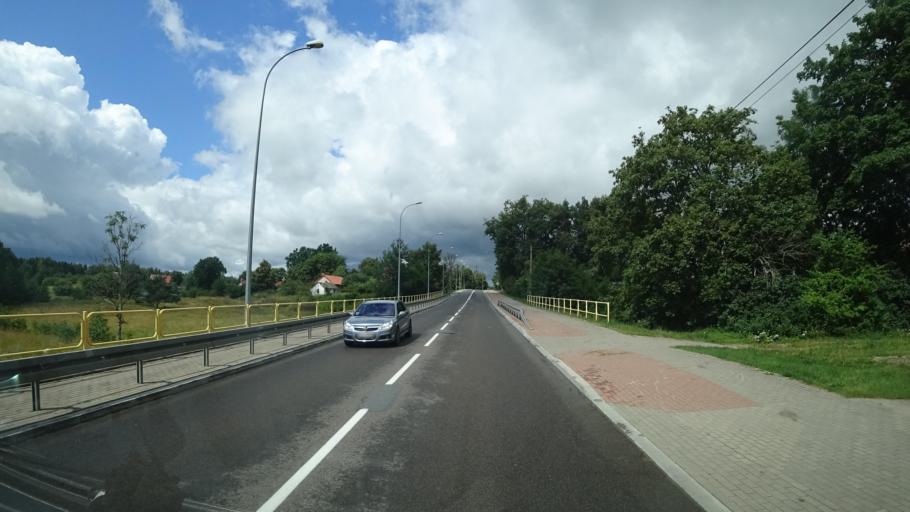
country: PL
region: Warmian-Masurian Voivodeship
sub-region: Powiat olecki
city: Kowale Oleckie
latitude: 54.1578
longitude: 22.4203
